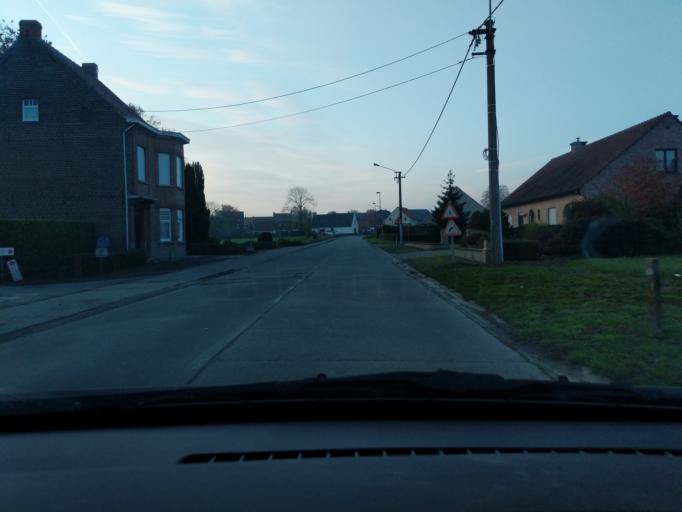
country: BE
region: Flanders
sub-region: Provincie Oost-Vlaanderen
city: Aalter
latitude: 51.0467
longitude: 3.4693
